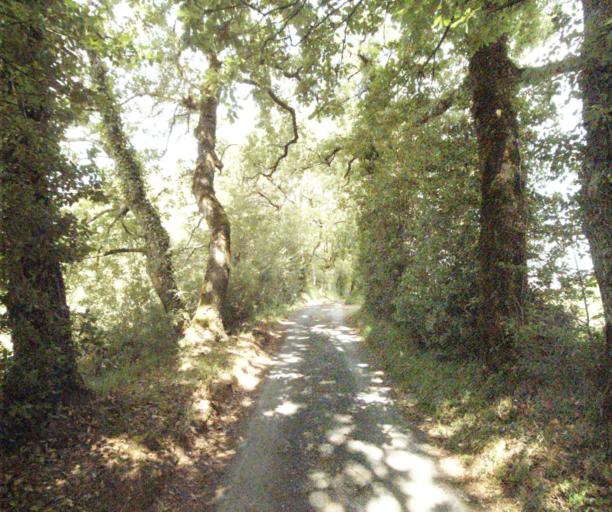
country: FR
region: Midi-Pyrenees
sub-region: Departement du Tarn
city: Soreze
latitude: 43.4591
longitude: 2.0956
